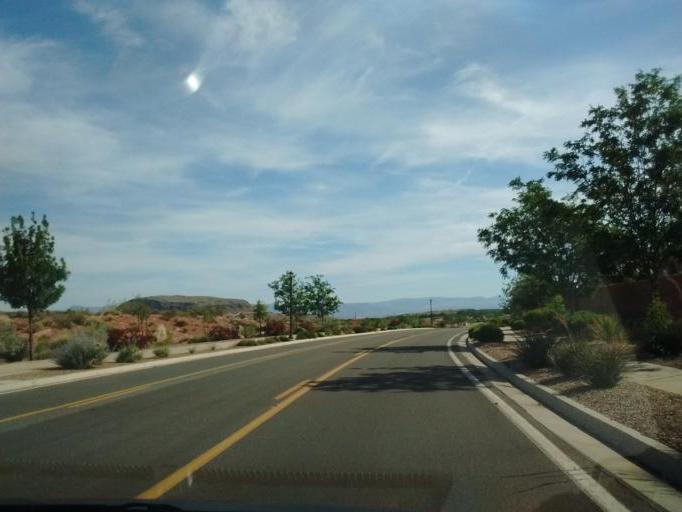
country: US
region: Utah
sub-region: Washington County
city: Washington
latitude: 37.1432
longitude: -113.4816
